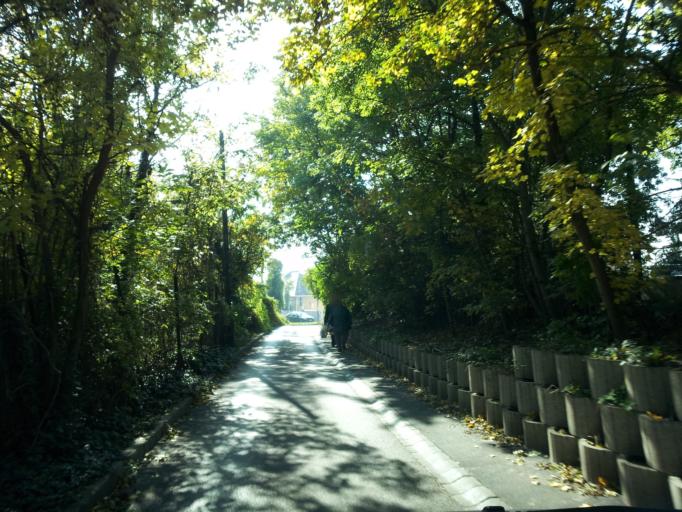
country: HU
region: Budapest
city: Budapest XII. keruelet
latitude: 47.4832
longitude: 18.9977
